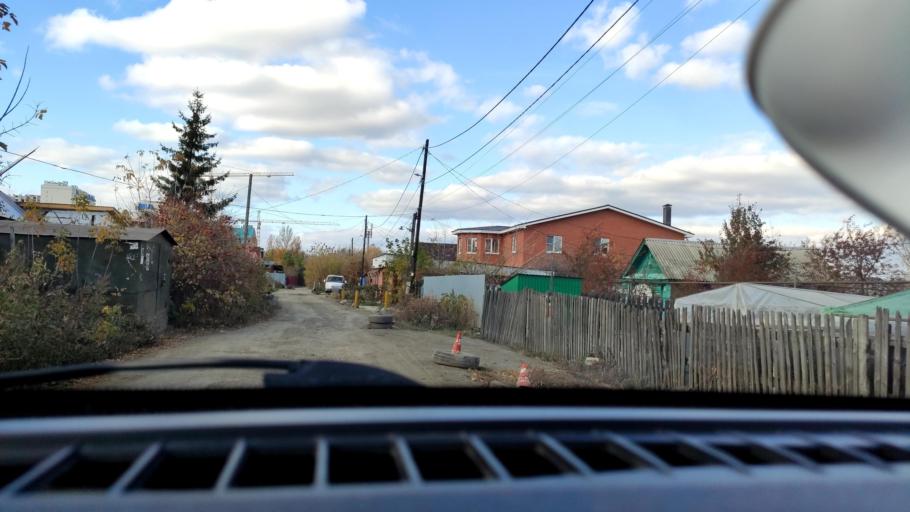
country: RU
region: Samara
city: Samara
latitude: 53.2206
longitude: 50.2102
